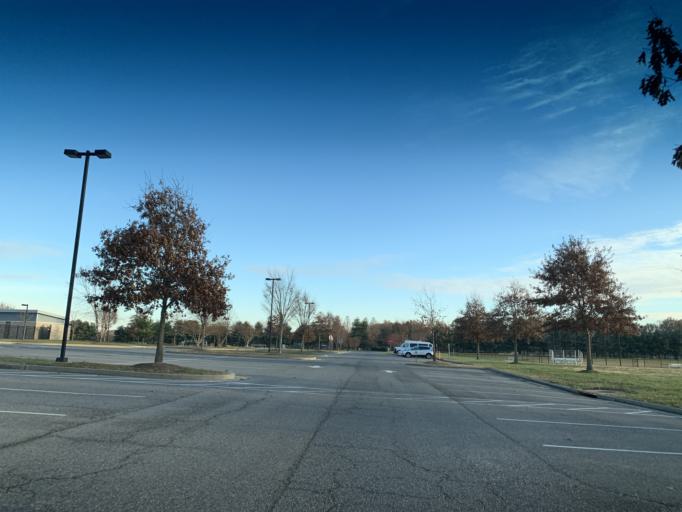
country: US
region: Maryland
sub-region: Kent County
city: Chestertown
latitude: 39.2817
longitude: -76.0931
